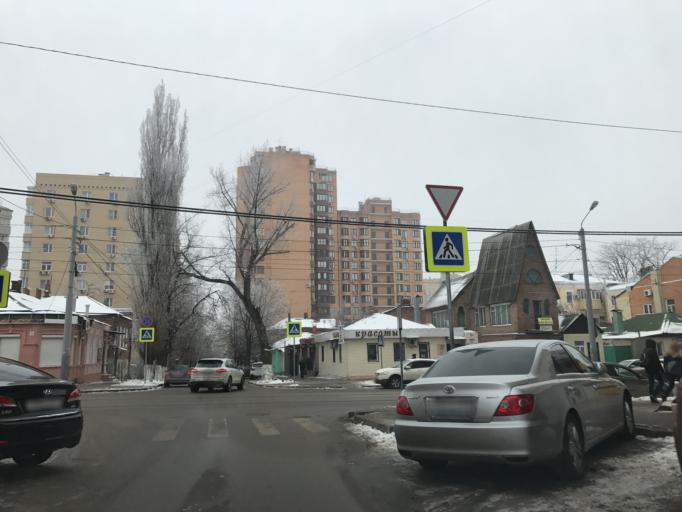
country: RU
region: Rostov
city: Rostov-na-Donu
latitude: 47.2240
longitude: 39.7006
